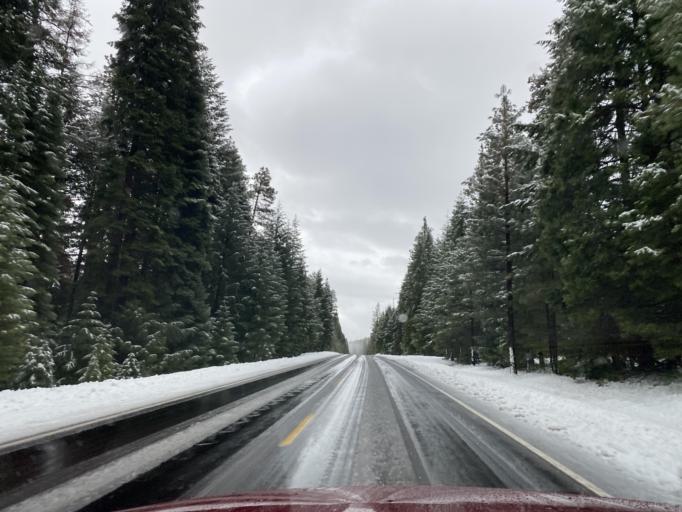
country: US
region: Oregon
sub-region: Klamath County
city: Klamath Falls
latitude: 42.5336
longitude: -122.0904
